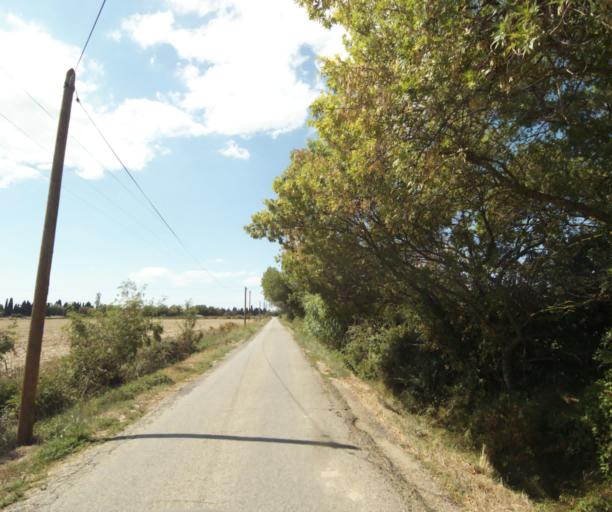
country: FR
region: Languedoc-Roussillon
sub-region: Departement du Gard
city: Caissargues
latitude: 43.8147
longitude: 4.4008
